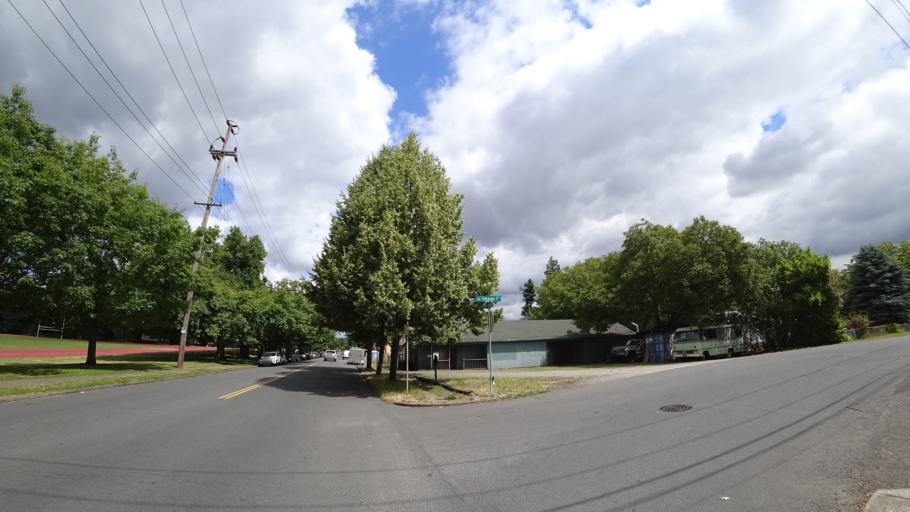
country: US
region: Oregon
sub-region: Multnomah County
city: Portland
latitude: 45.5650
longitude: -122.6204
